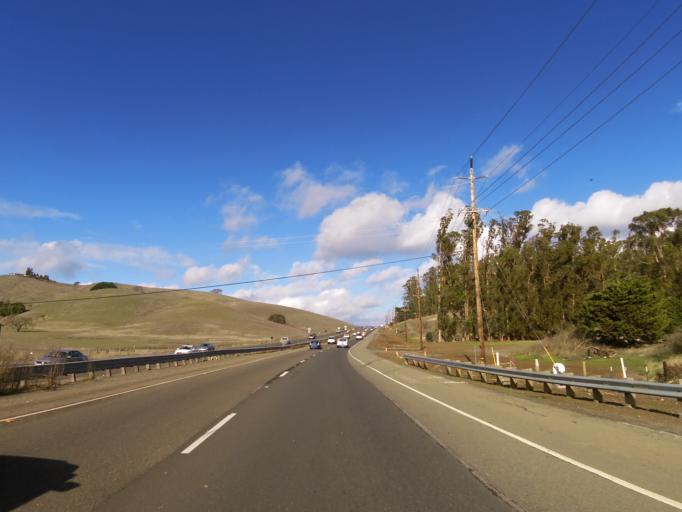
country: US
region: California
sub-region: Sonoma County
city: Petaluma
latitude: 38.1899
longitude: -122.6010
